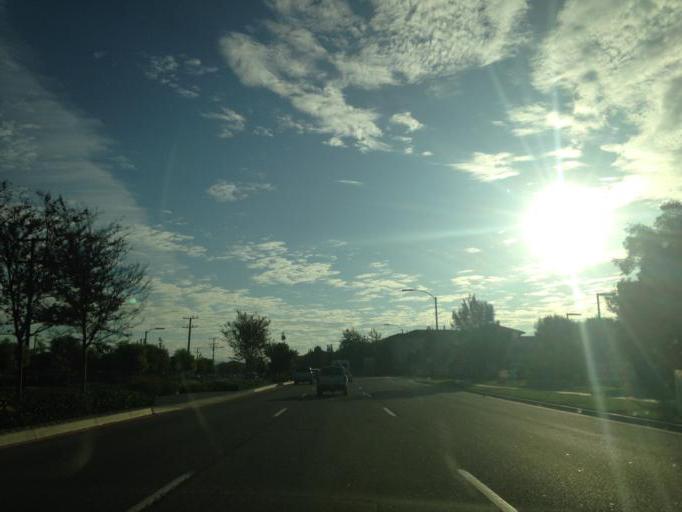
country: US
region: California
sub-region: Riverside County
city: Temecula
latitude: 33.4759
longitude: -117.1214
